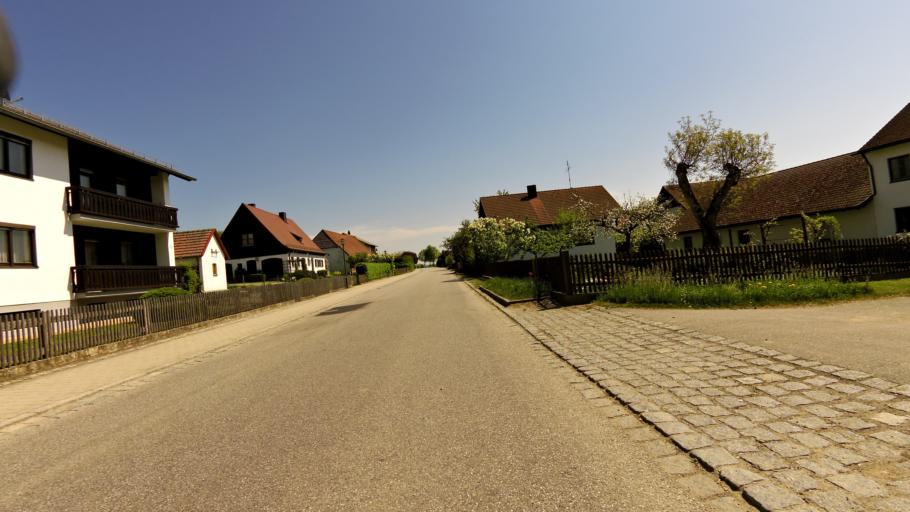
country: DE
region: Bavaria
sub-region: Lower Bavaria
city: Weihmichl
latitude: 48.5735
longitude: 12.0785
